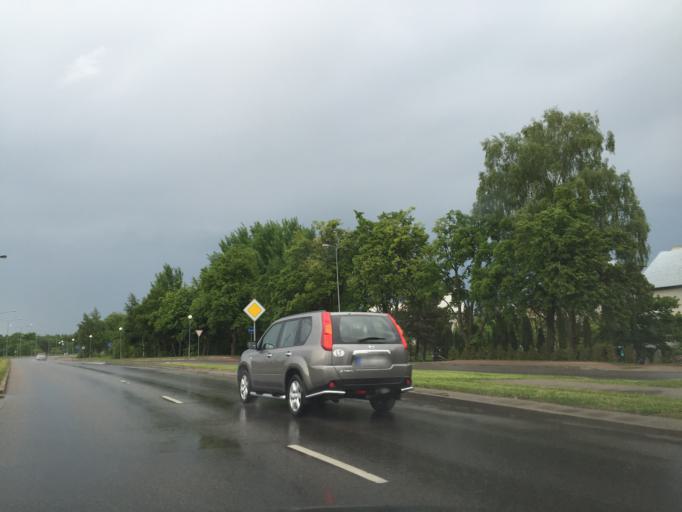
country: LT
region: Klaipedos apskritis
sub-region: Klaipeda
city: Klaipeda
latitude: 55.7555
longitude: 21.1303
